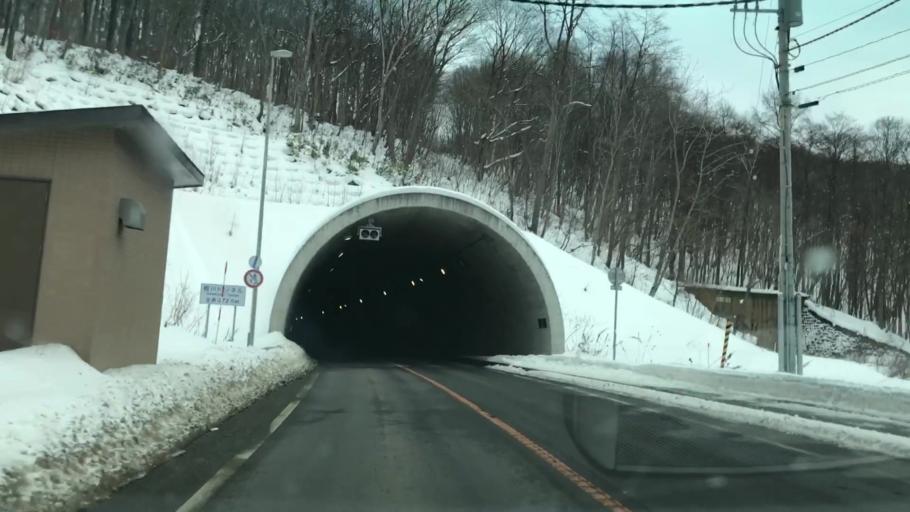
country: JP
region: Hokkaido
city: Yoichi
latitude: 43.2217
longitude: 140.7369
